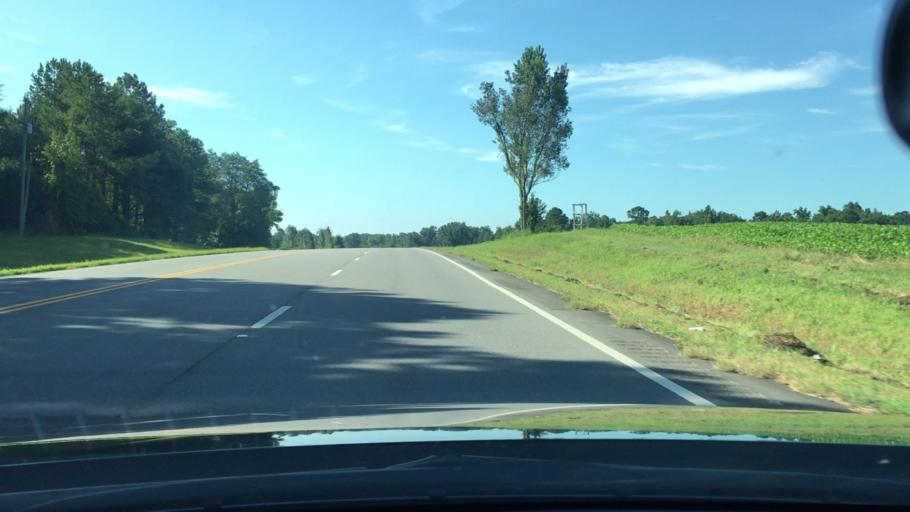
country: US
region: Georgia
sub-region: Putnam County
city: Jefferson
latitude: 33.4498
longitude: -83.4076
